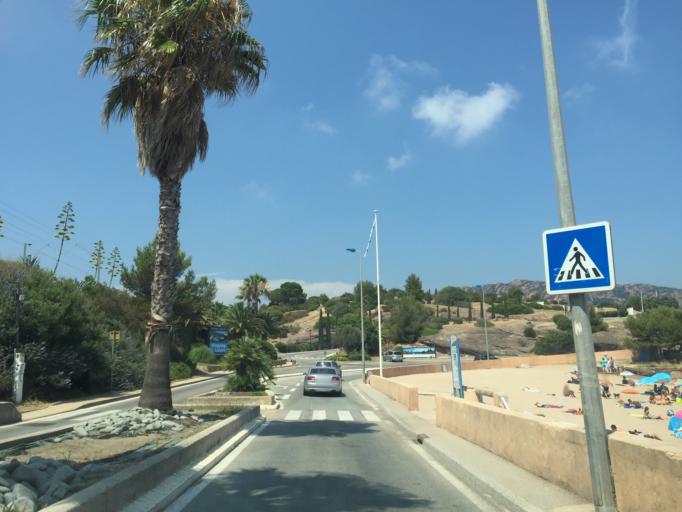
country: FR
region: Provence-Alpes-Cote d'Azur
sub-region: Departement du Var
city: Saint-Raphael
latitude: 43.4251
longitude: 6.8559
